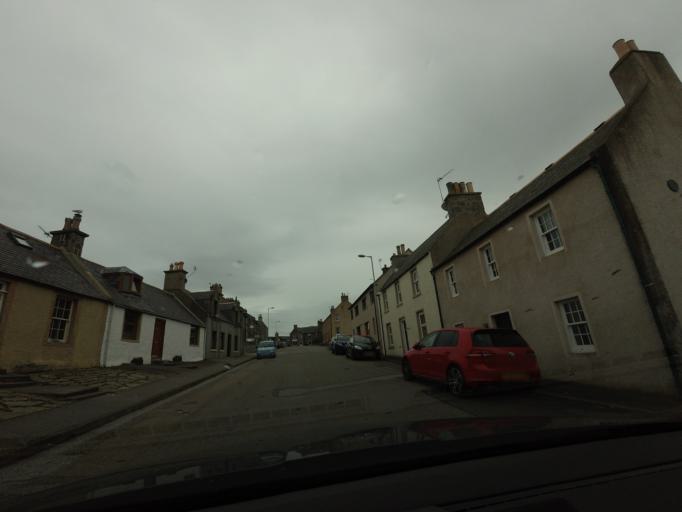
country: GB
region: Scotland
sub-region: Aberdeenshire
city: Portsoy
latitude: 57.6824
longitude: -2.6886
